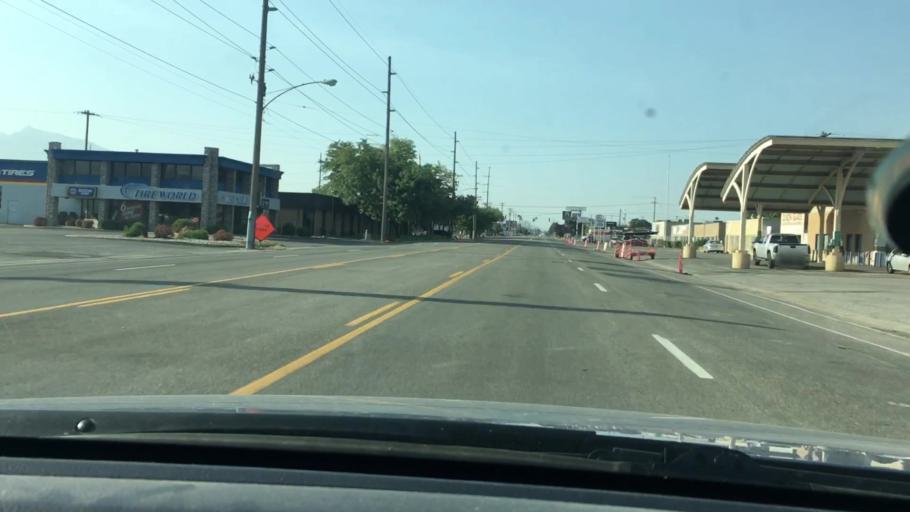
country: US
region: Utah
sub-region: Salt Lake County
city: South Salt Lake
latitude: 40.7150
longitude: -111.8998
